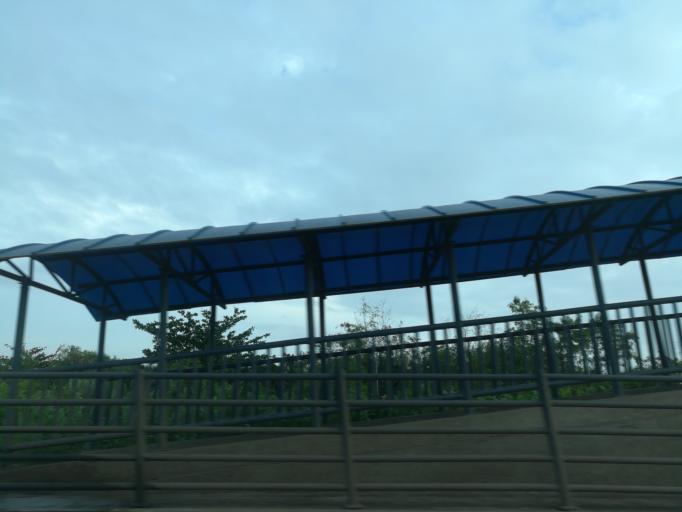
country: NG
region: Lagos
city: Ebute Ikorodu
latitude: 6.6189
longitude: 3.4631
